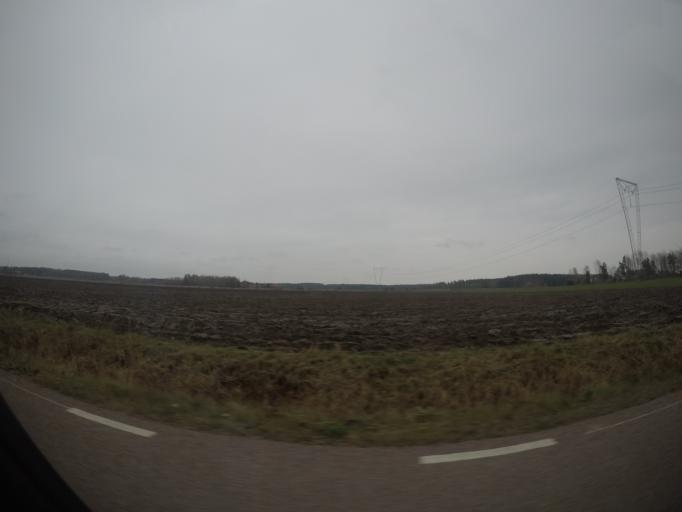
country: SE
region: Vaestmanland
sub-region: Kopings Kommun
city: Koping
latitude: 59.5515
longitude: 16.1073
